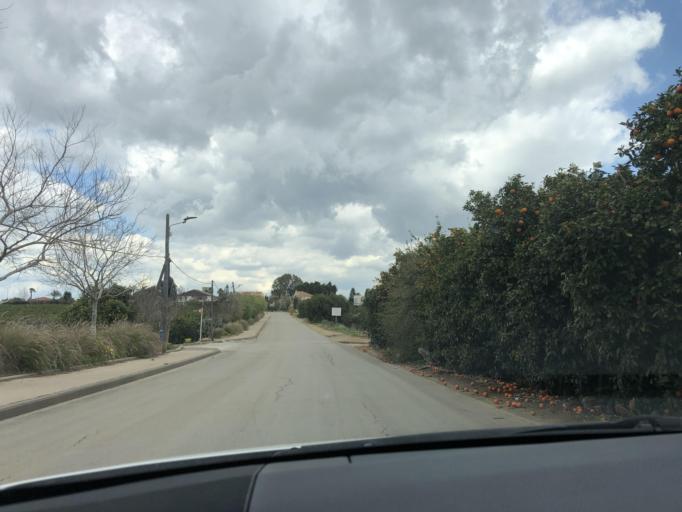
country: IL
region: Central District
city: Tel Mond
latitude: 32.2696
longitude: 34.9356
